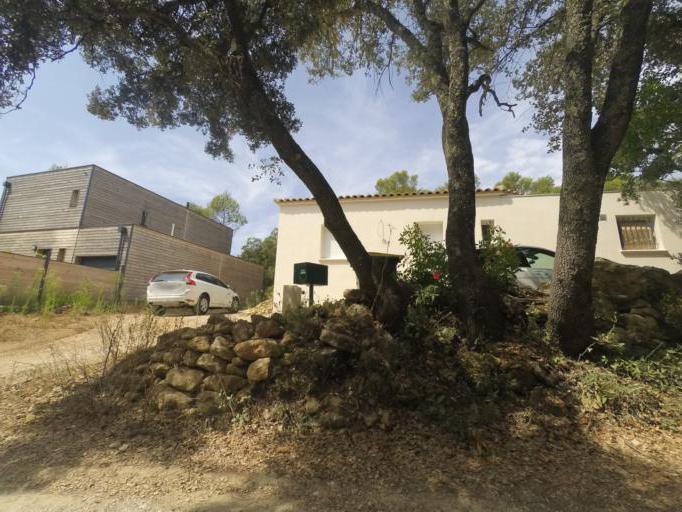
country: FR
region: Languedoc-Roussillon
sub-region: Departement du Gard
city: Aubais
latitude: 43.7551
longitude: 4.1407
